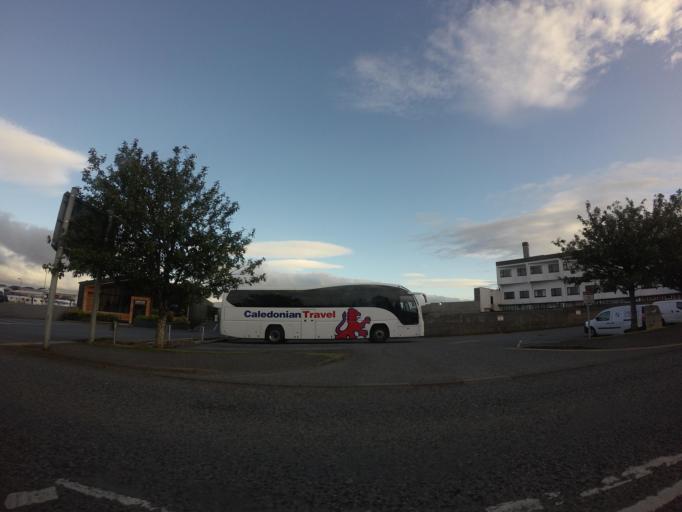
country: GB
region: Scotland
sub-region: Eilean Siar
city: Stornoway
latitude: 58.2086
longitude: -6.3805
